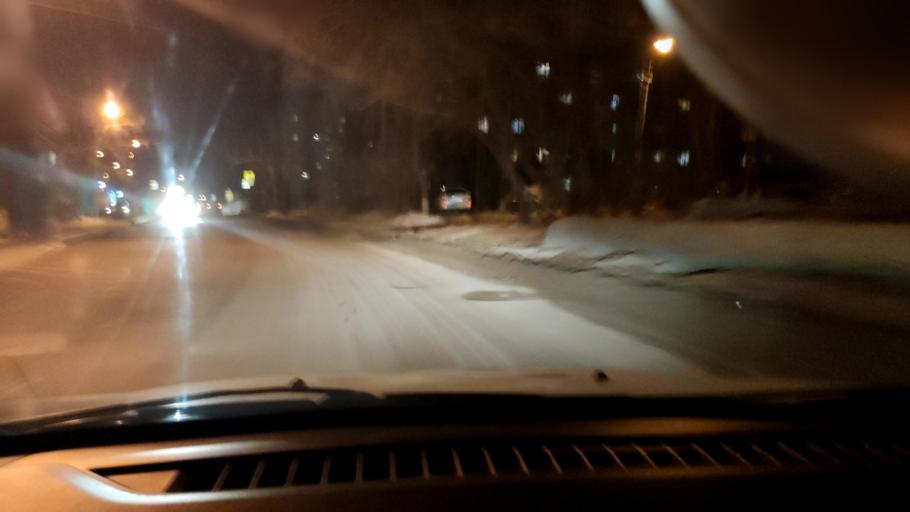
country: RU
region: Perm
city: Overyata
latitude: 58.0264
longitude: 55.8444
